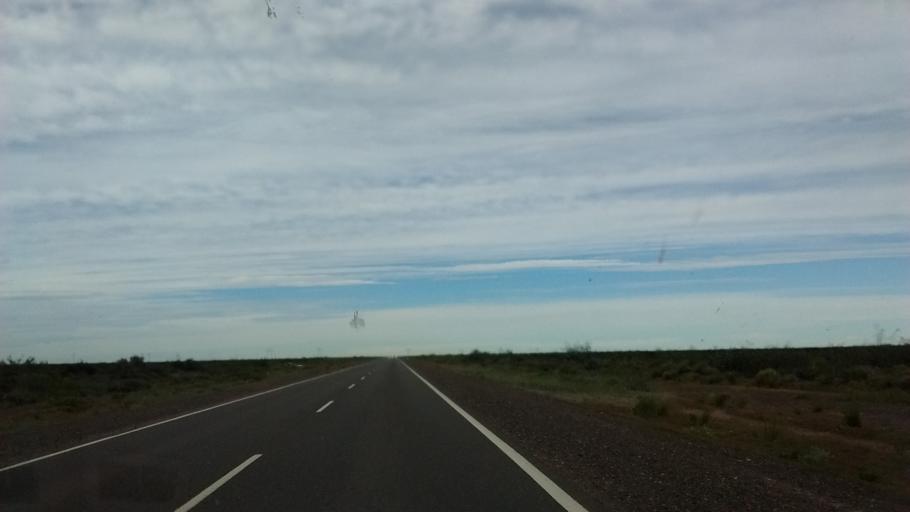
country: AR
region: Rio Negro
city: Contraalmirante Cordero
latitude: -38.5500
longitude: -68.0865
